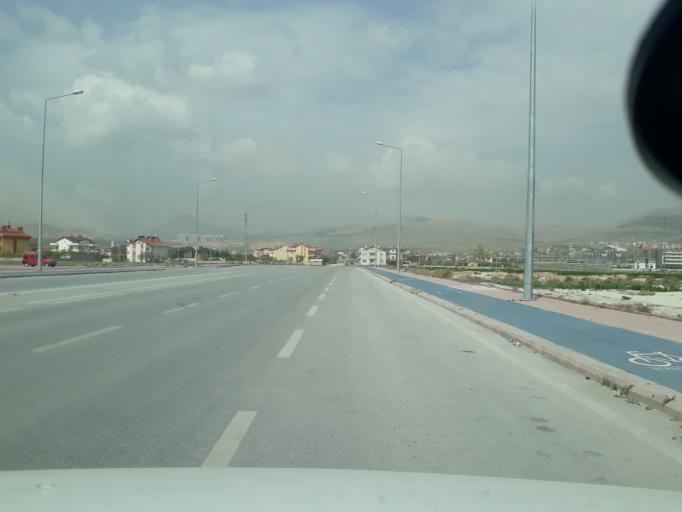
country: TR
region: Konya
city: Selcuklu
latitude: 37.9424
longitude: 32.4840
